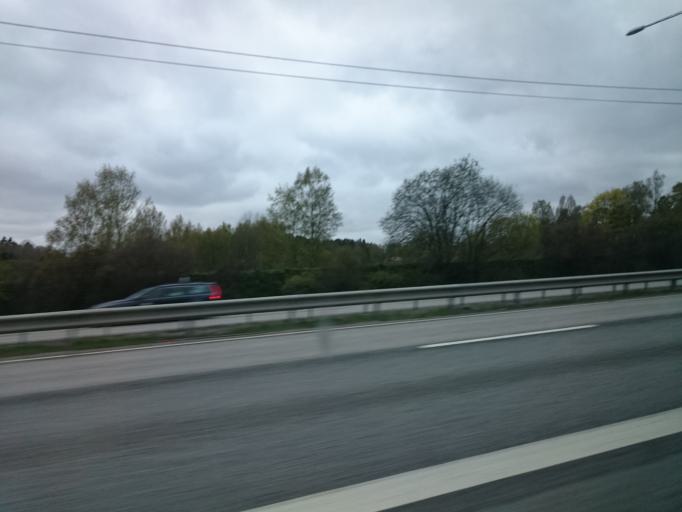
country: SE
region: Stockholm
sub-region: Stockholms Kommun
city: Arsta
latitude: 59.2537
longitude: 18.1001
